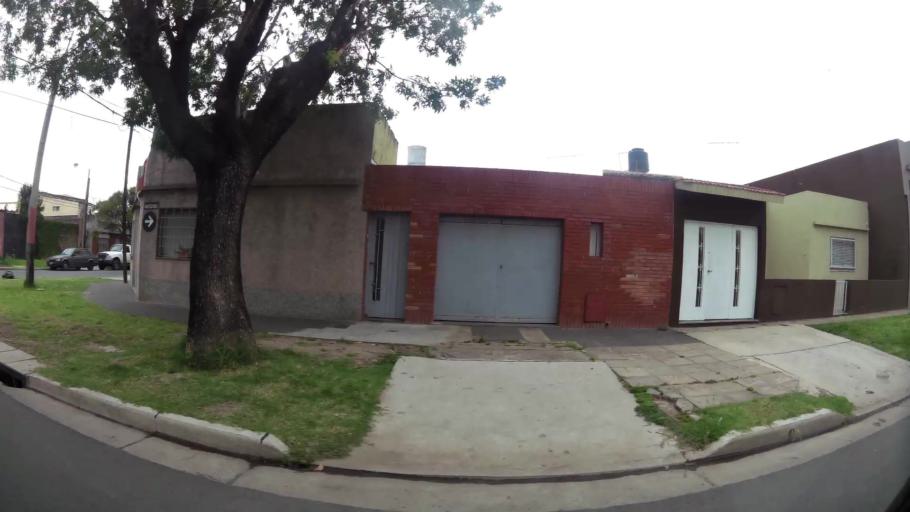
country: AR
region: Santa Fe
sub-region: Departamento de Rosario
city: Rosario
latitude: -32.9854
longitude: -60.6584
